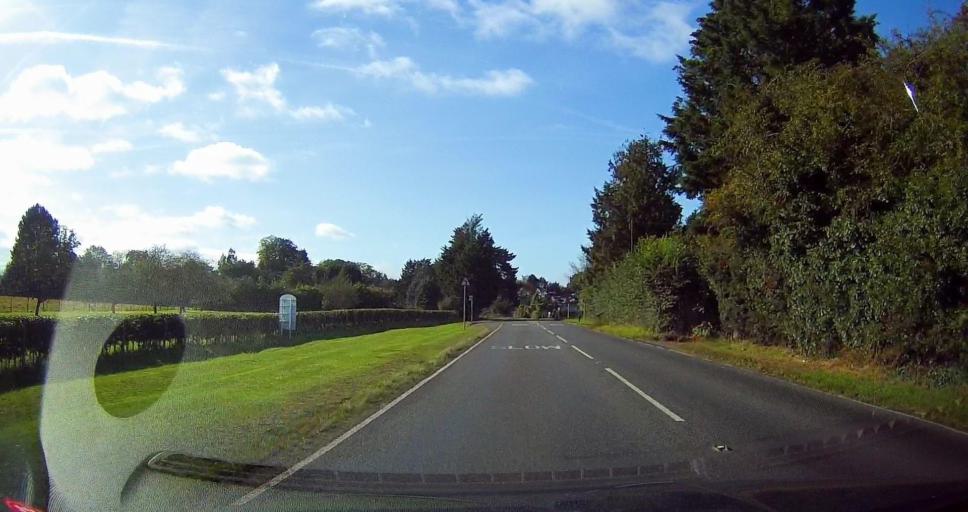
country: GB
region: England
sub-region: Kent
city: Hadlow
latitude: 51.2176
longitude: 0.3144
